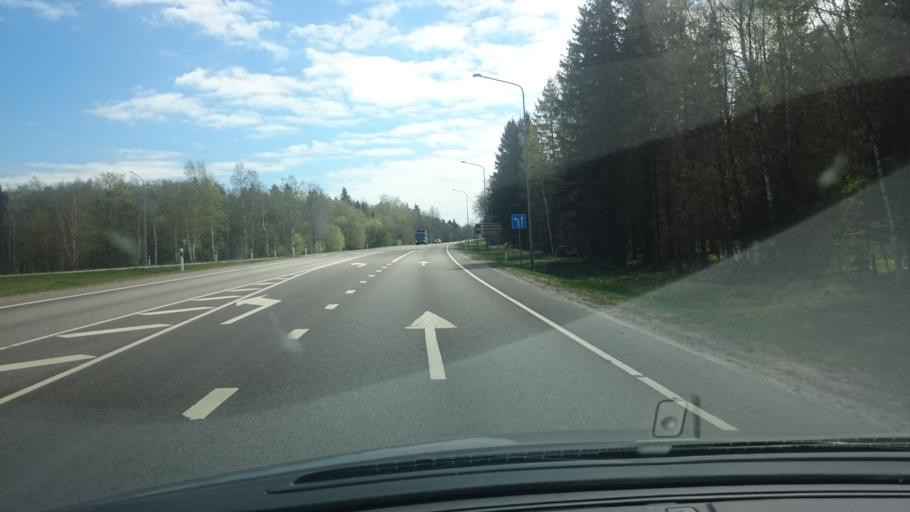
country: EE
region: Ida-Virumaa
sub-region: Kohtla-Jaerve linn
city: Kohtla-Jarve
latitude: 59.4192
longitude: 27.2835
